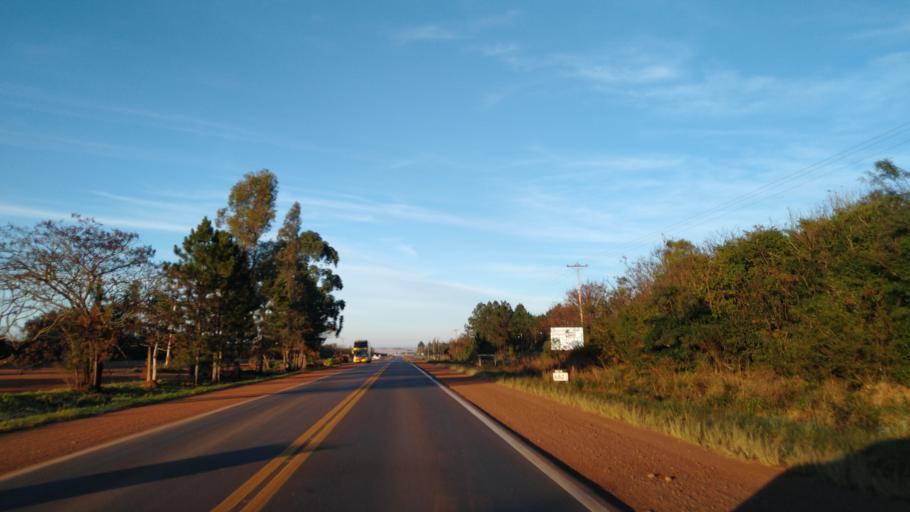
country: AR
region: Corrientes
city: Santo Tome
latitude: -28.5773
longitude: -56.0845
